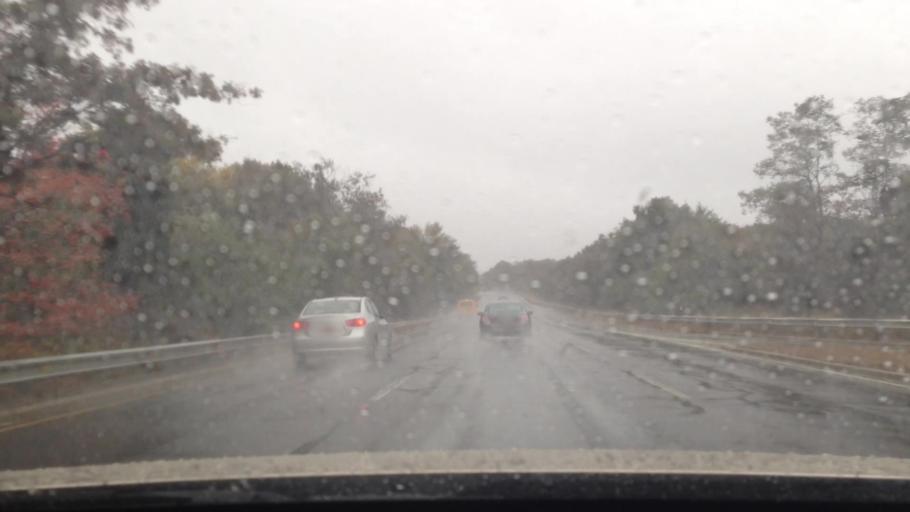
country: US
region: New York
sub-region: Suffolk County
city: Farmingville
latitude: 40.8449
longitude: -73.0181
